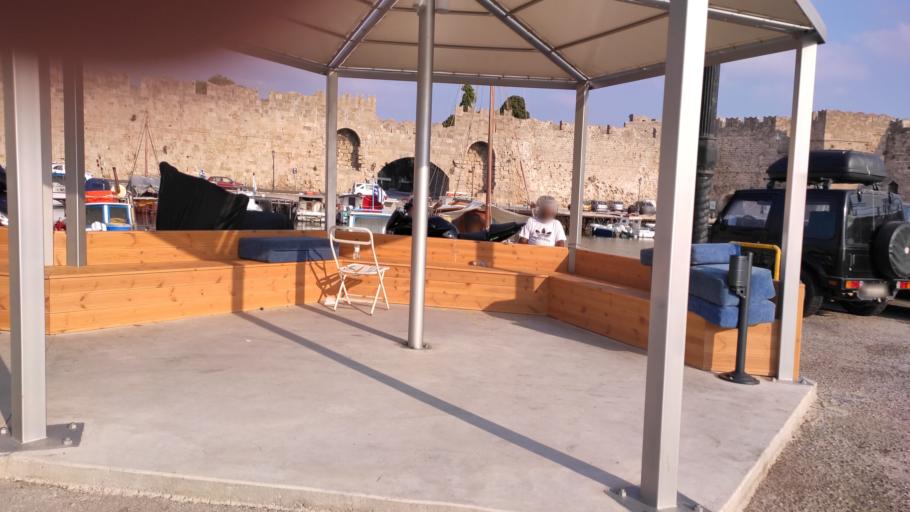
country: GR
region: South Aegean
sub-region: Nomos Dodekanisou
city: Rodos
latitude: 36.4456
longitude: 28.2288
